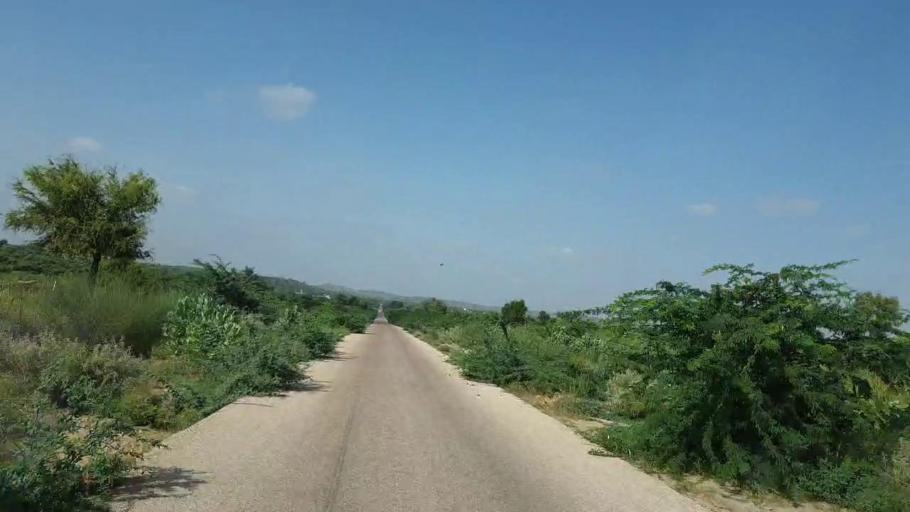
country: PK
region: Sindh
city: Mithi
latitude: 24.5353
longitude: 69.8547
